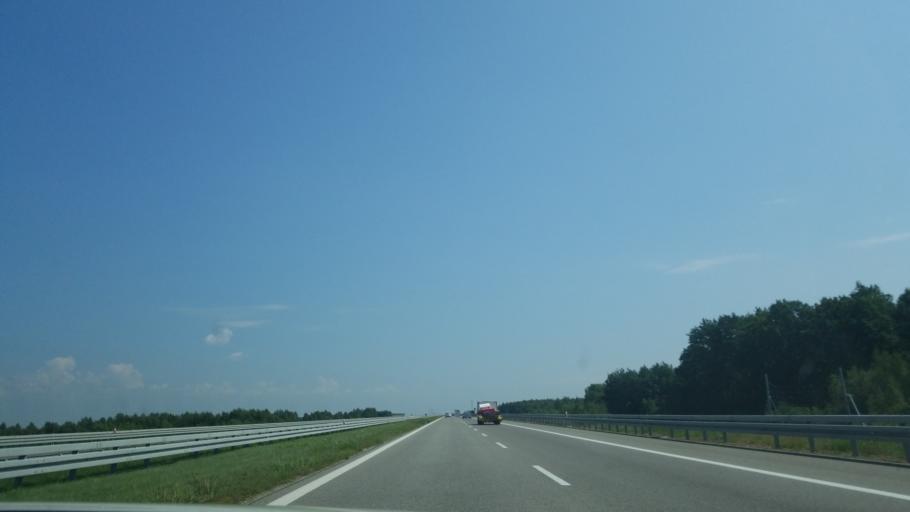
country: PL
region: Subcarpathian Voivodeship
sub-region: Powiat rzeszowski
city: Trzciana
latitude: 50.1146
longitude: 21.8213
